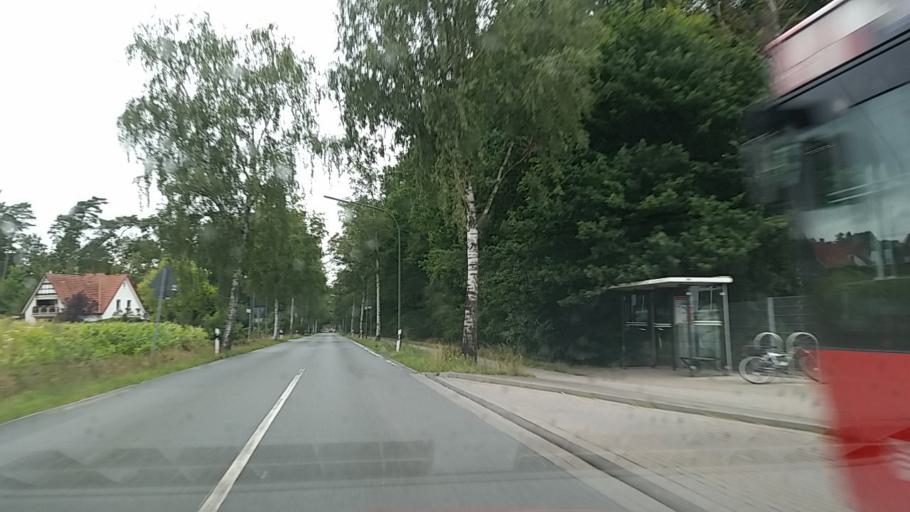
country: DE
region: North Rhine-Westphalia
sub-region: Regierungsbezirk Munster
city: Lotte
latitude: 52.2741
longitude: 7.9559
